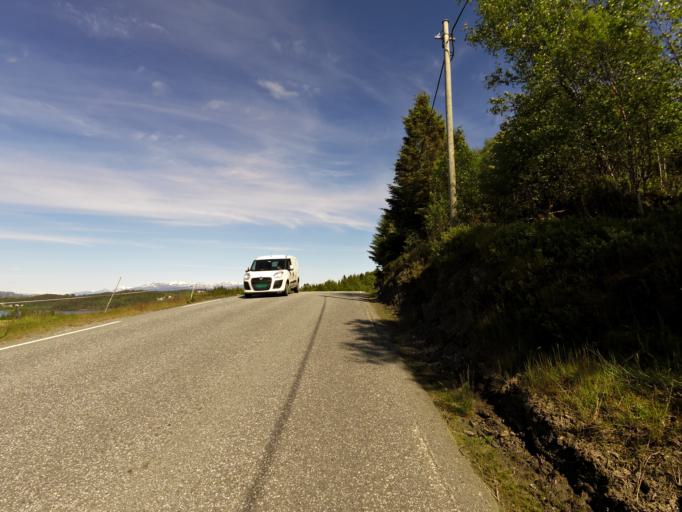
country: NO
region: Hordaland
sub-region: Stord
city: Leirvik
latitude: 59.7880
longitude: 5.4724
